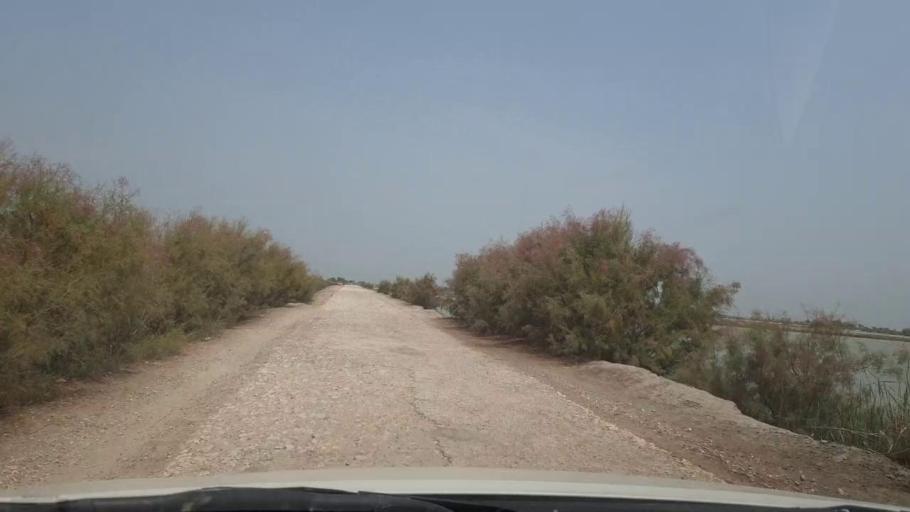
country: PK
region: Sindh
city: Rustam jo Goth
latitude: 28.0650
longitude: 68.8169
